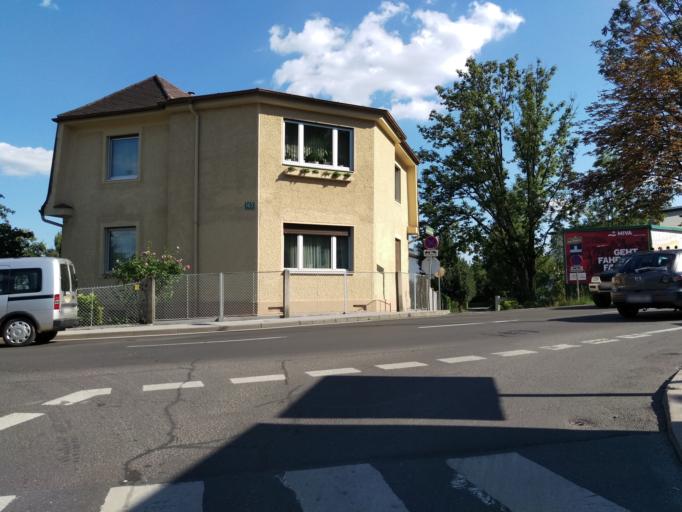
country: AT
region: Styria
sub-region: Graz Stadt
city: Wetzelsdorf
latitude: 47.0595
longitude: 15.3910
